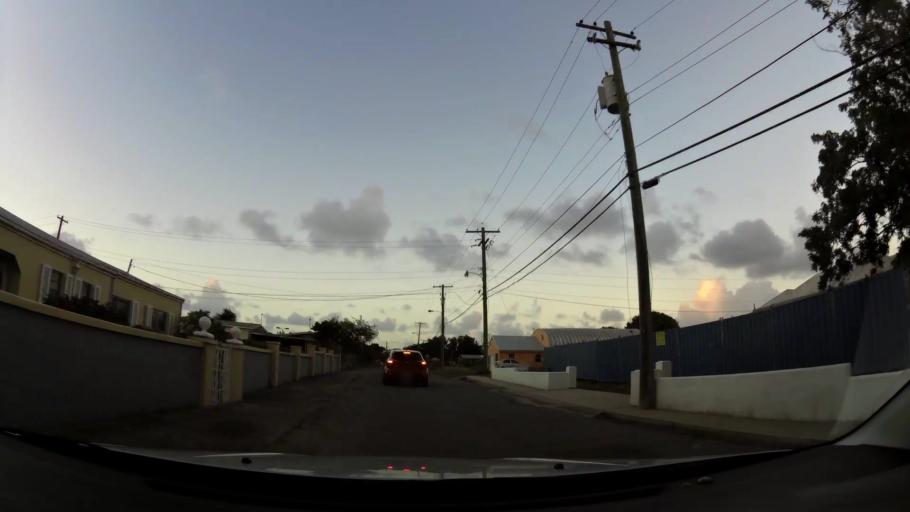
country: AG
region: Saint John
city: Saint John's
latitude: 17.1244
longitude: -61.8360
